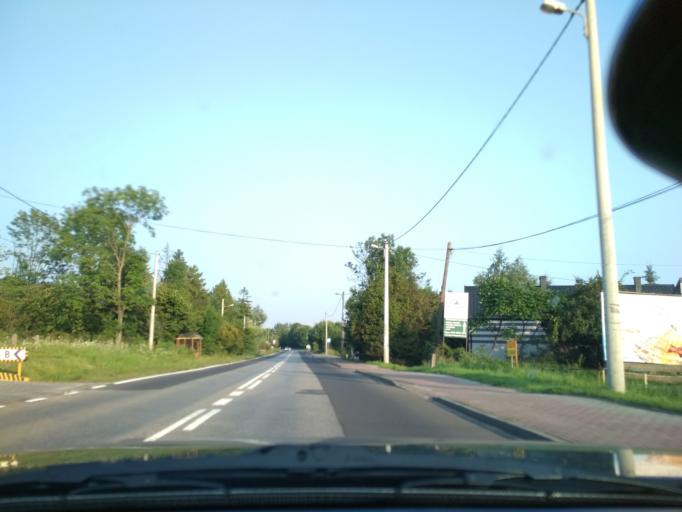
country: PL
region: Silesian Voivodeship
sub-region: Powiat zawiercianski
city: Ogrodzieniec
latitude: 50.4568
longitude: 19.5018
